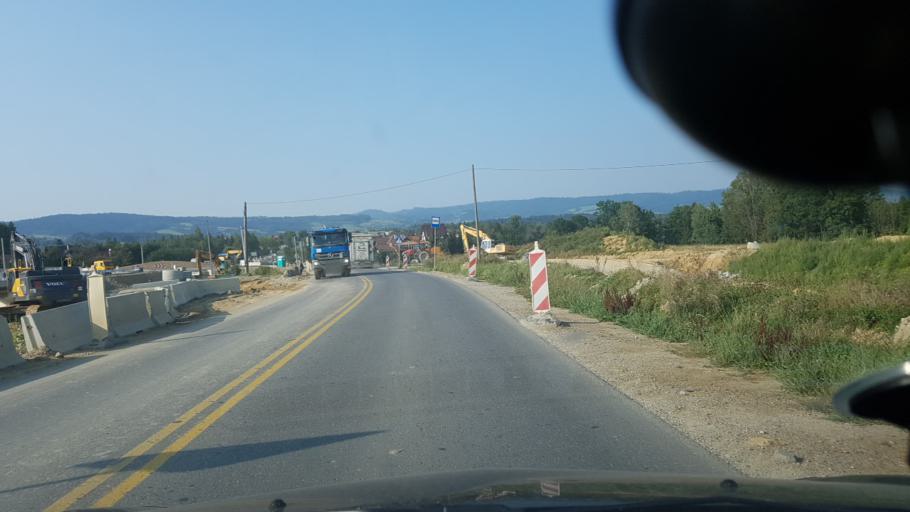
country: PL
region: Lesser Poland Voivodeship
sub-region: Powiat nowotarski
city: Rokiciny
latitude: 49.6050
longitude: 19.9248
